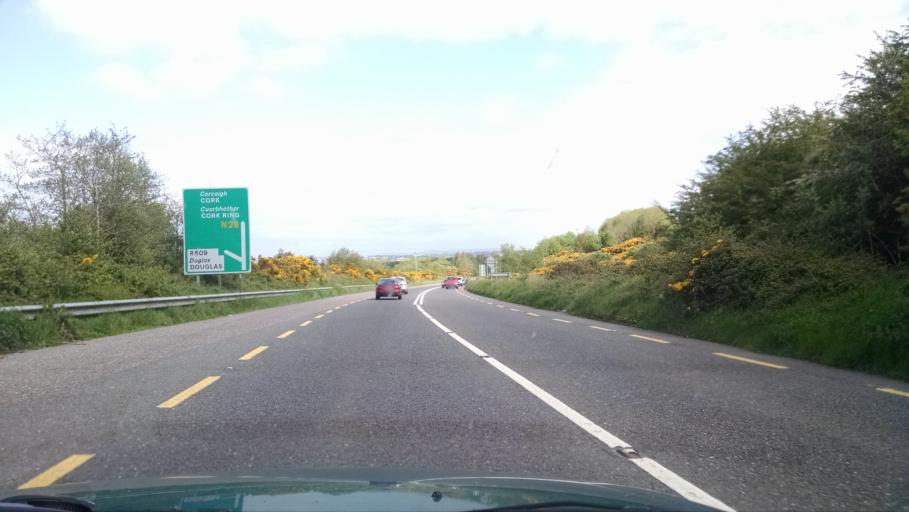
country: IE
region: Munster
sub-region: County Cork
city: Carrigaline
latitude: 51.8559
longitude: -8.4208
